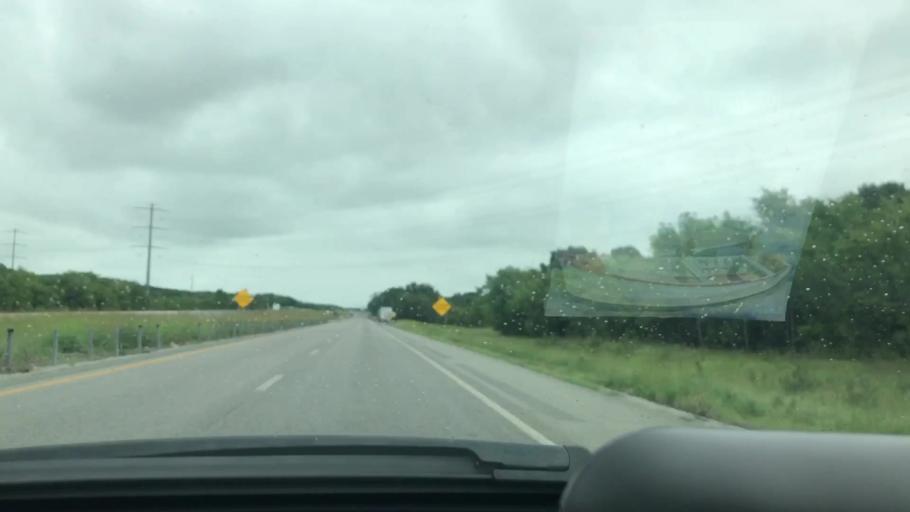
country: US
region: Oklahoma
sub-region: Coal County
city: Coalgate
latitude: 34.6232
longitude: -95.9626
